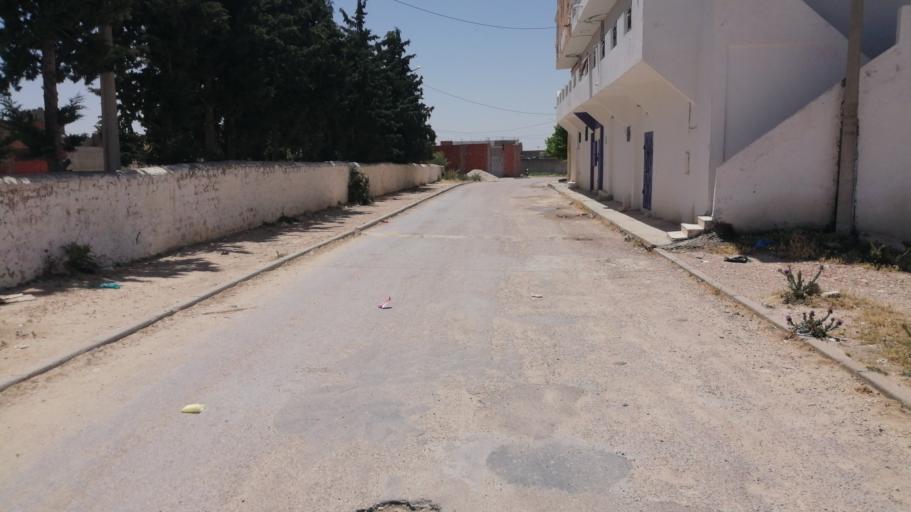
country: TN
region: Silyanah
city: Maktar
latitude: 35.8518
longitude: 9.2036
